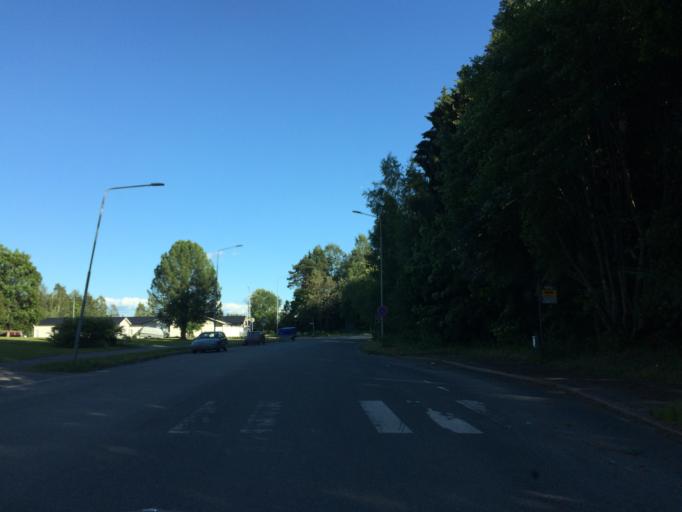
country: FI
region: Haeme
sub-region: Haemeenlinna
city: Haemeenlinna
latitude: 60.9971
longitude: 24.5022
